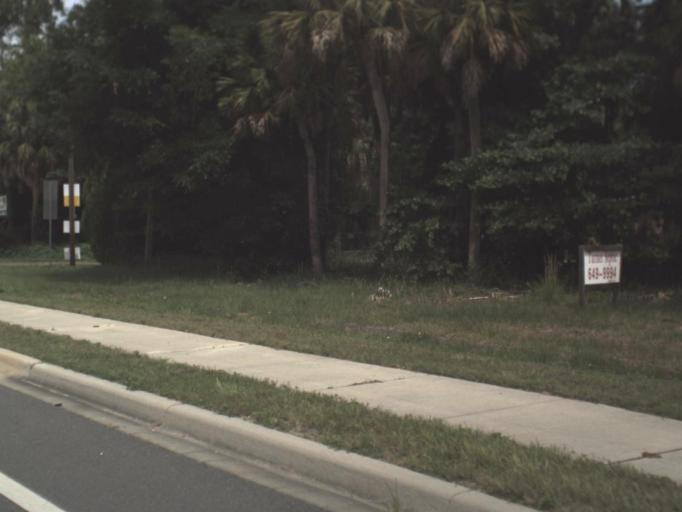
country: US
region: Florida
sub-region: Putnam County
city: Interlachen
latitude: 29.6280
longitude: -81.8433
